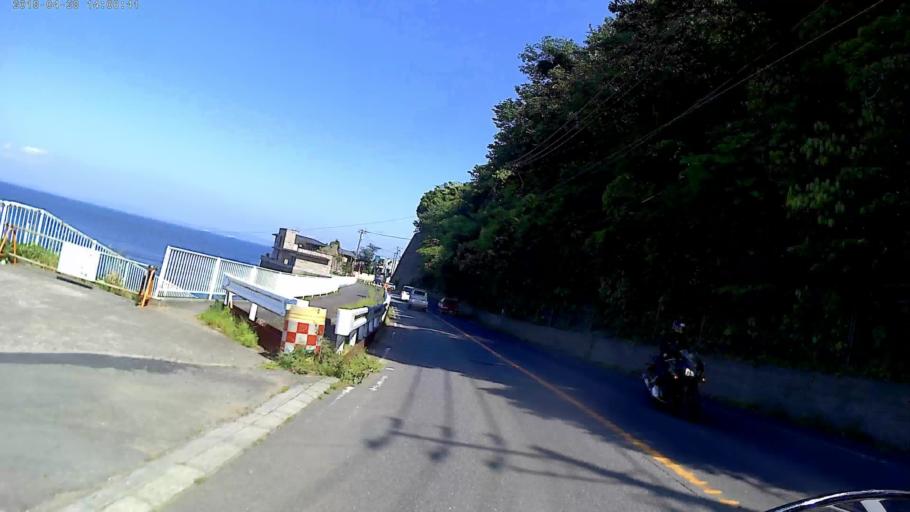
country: JP
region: Kanagawa
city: Miura
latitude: 35.1719
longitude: 139.6574
